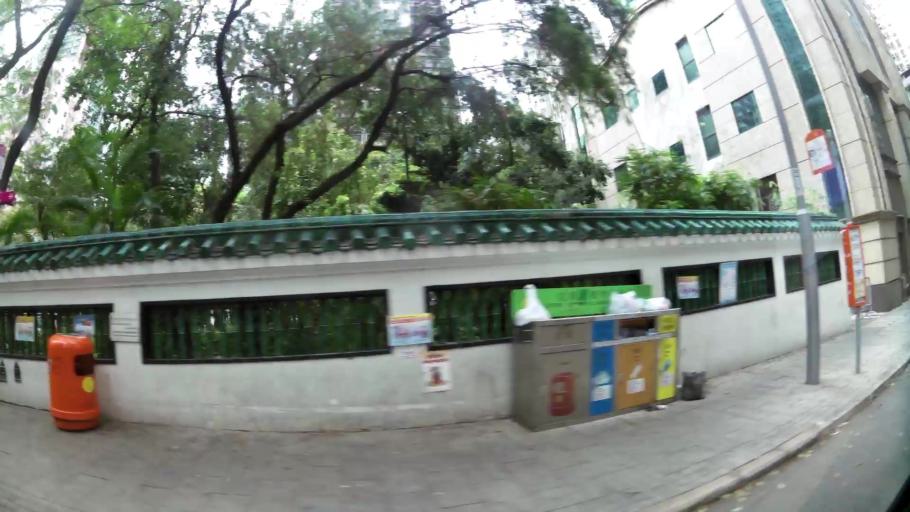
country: HK
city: Hong Kong
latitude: 22.2862
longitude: 114.1472
